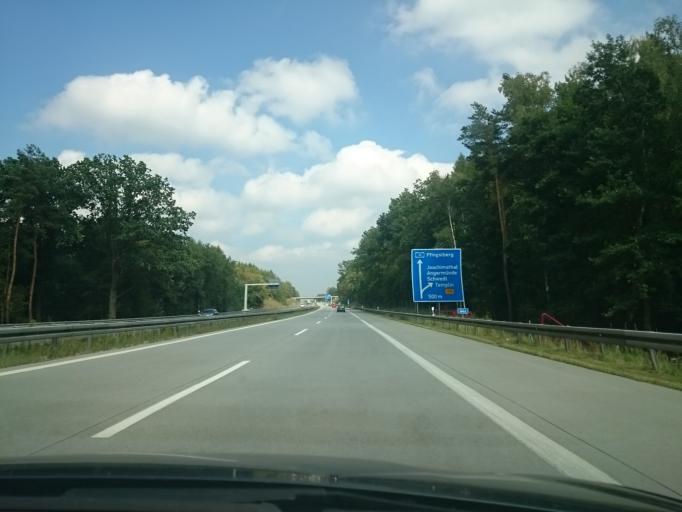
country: DE
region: Brandenburg
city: Althuttendorf
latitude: 52.9471
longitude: 13.8018
